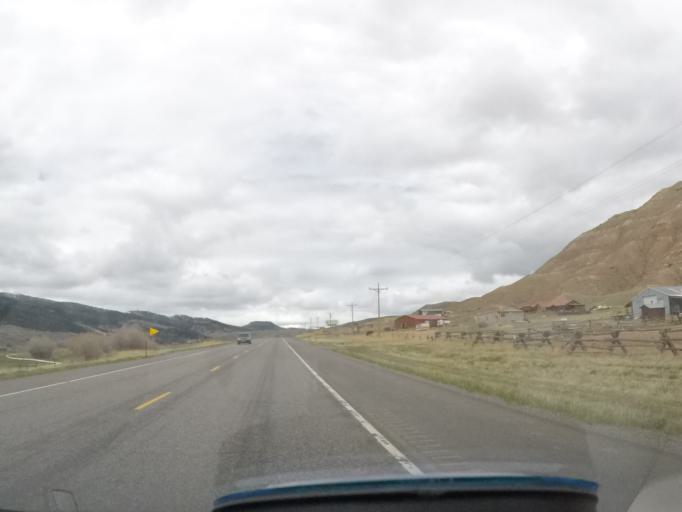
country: US
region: Wyoming
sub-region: Sublette County
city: Pinedale
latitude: 43.5707
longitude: -109.7185
